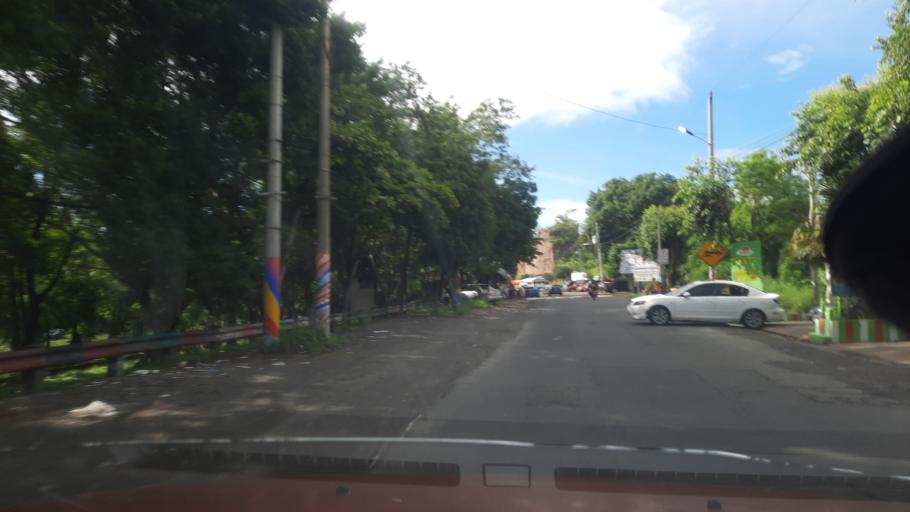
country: SV
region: La Paz
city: Olocuilta
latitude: 13.5651
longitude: -89.1181
